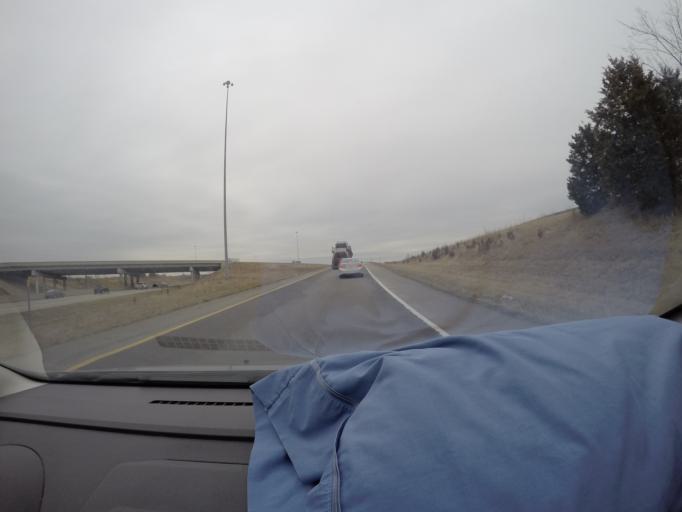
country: US
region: Missouri
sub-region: Saint Charles County
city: Wentzville
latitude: 38.8059
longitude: -90.8404
